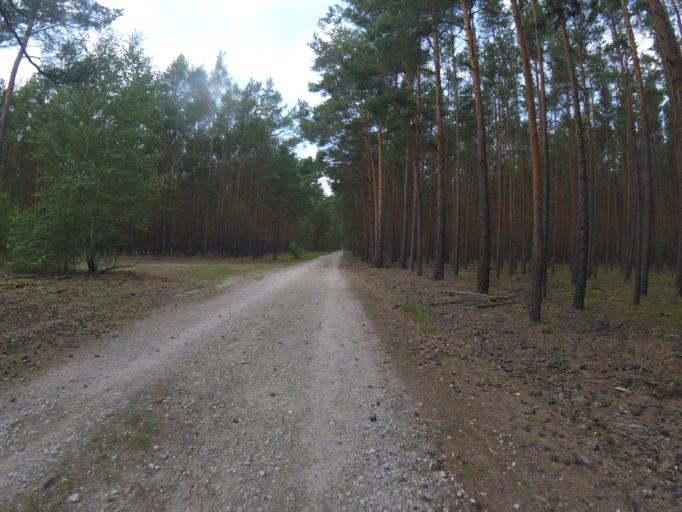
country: DE
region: Brandenburg
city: Schwerin
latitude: 52.1779
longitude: 13.6060
